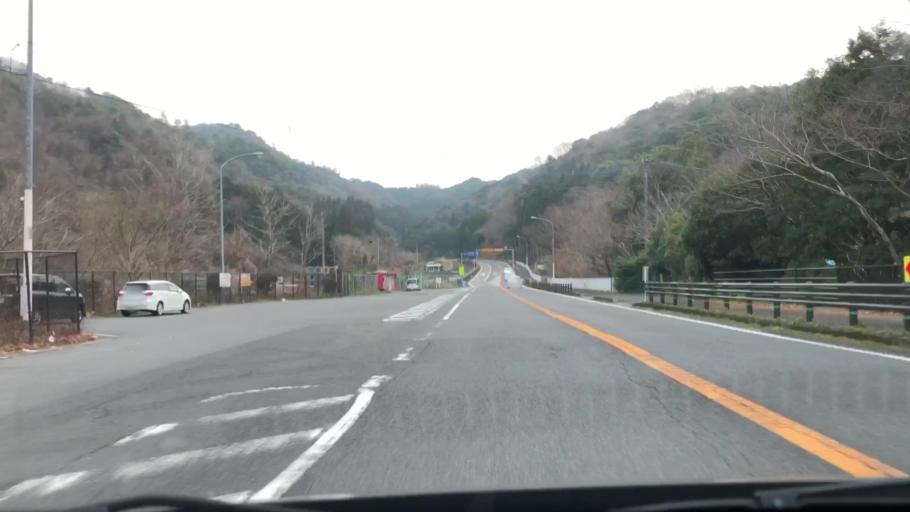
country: JP
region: Oita
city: Tsukumiura
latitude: 32.9958
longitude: 131.7607
